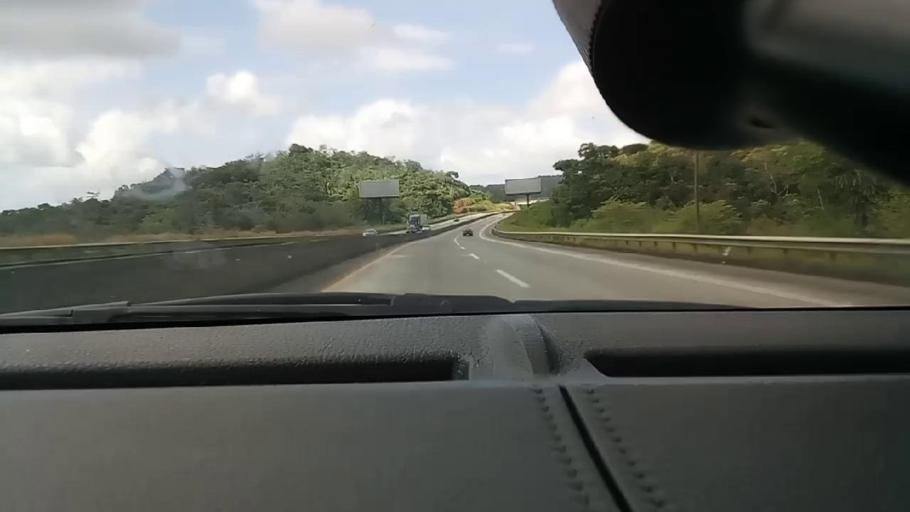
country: PA
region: Colon
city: Gatun
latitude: 9.2803
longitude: -79.7584
